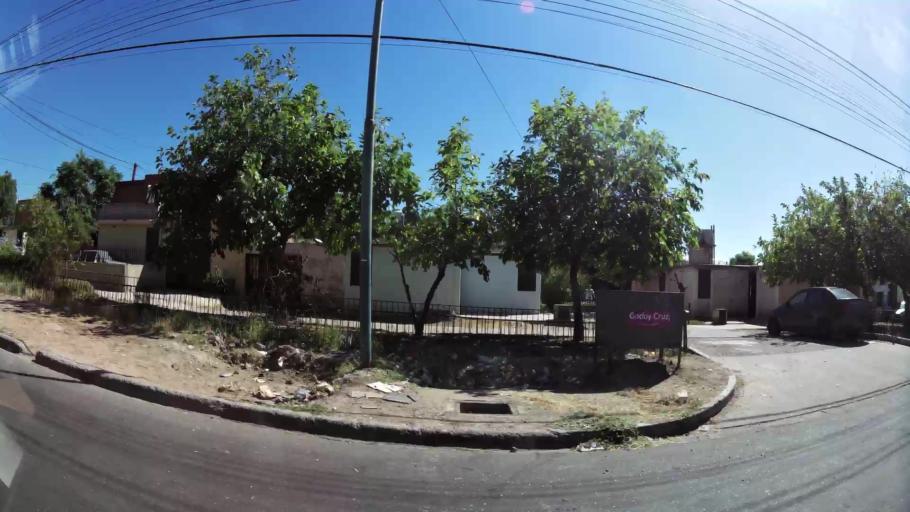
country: AR
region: Mendoza
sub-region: Departamento de Godoy Cruz
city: Godoy Cruz
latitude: -32.9075
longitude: -68.8726
